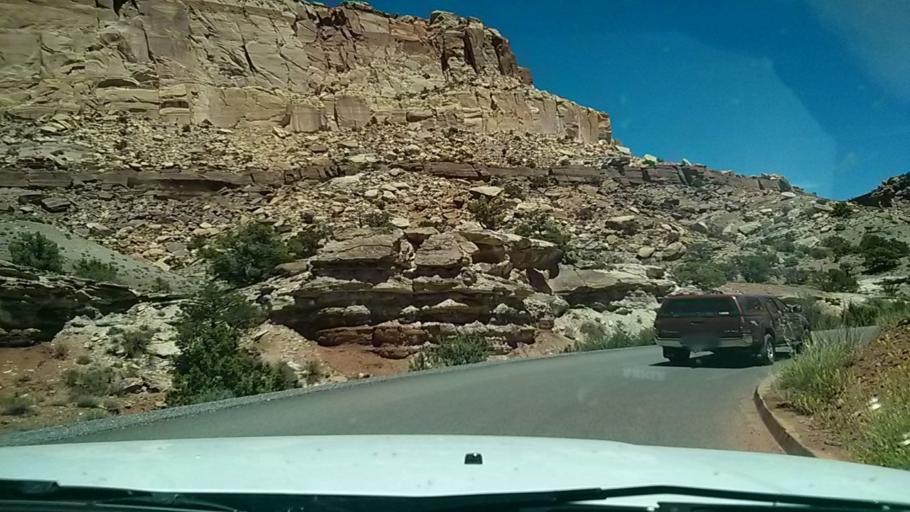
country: US
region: Utah
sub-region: Wayne County
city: Loa
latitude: 38.2097
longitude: -111.2014
